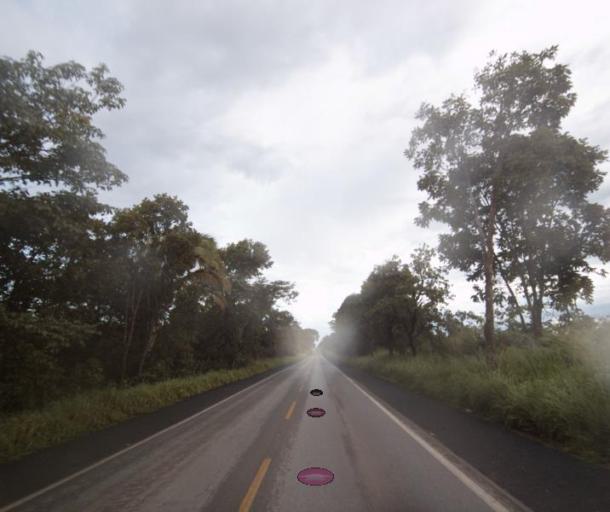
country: BR
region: Goias
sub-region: Porangatu
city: Porangatu
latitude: -13.8941
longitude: -49.0581
